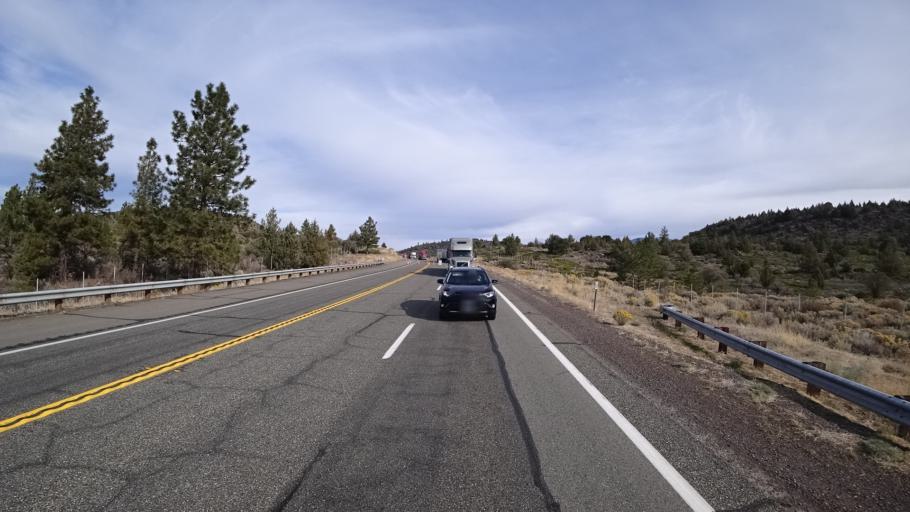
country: US
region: California
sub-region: Siskiyou County
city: Weed
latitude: 41.5242
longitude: -122.2850
